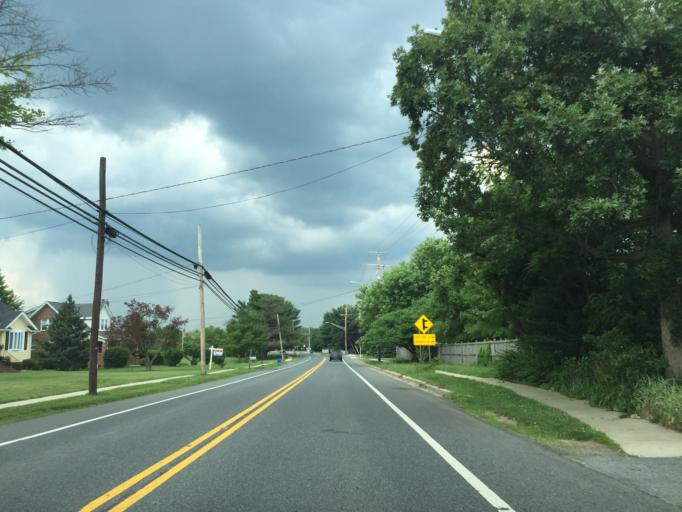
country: US
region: Maryland
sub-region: Montgomery County
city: Burtonsville
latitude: 39.0993
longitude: -76.9435
